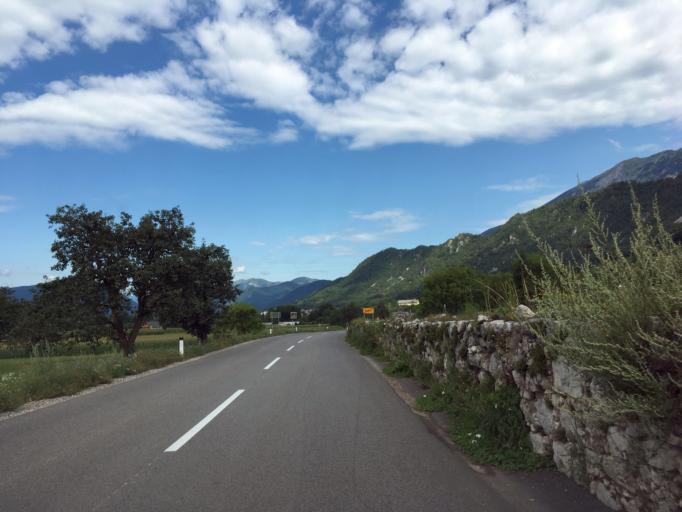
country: SI
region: Radovljica
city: Lesce
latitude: 46.3832
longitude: 14.1736
